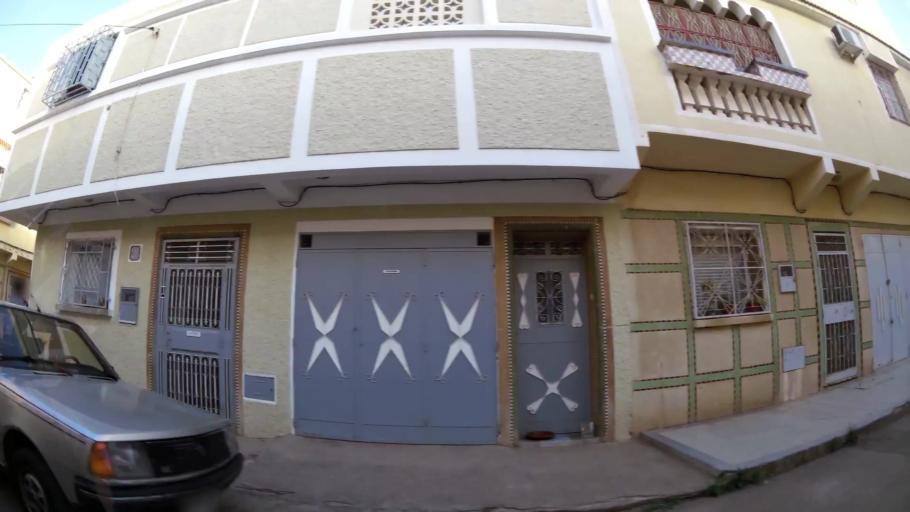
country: MA
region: Oriental
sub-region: Oujda-Angad
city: Oujda
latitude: 34.6750
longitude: -1.8938
